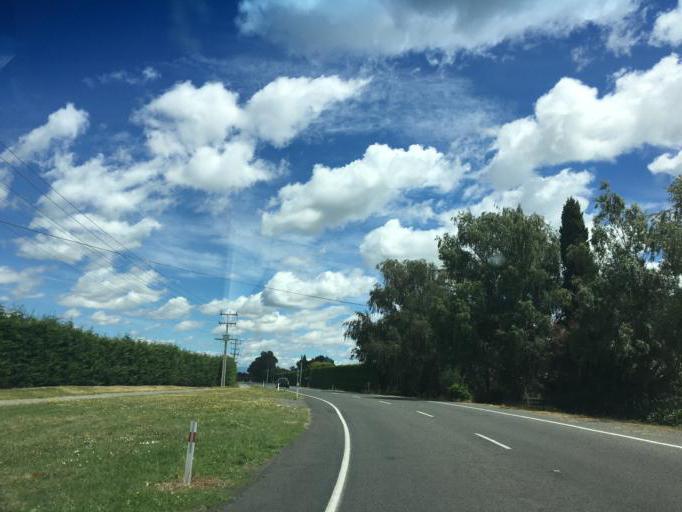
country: NZ
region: Hawke's Bay
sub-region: Hastings District
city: Hastings
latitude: -39.6560
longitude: 176.8799
